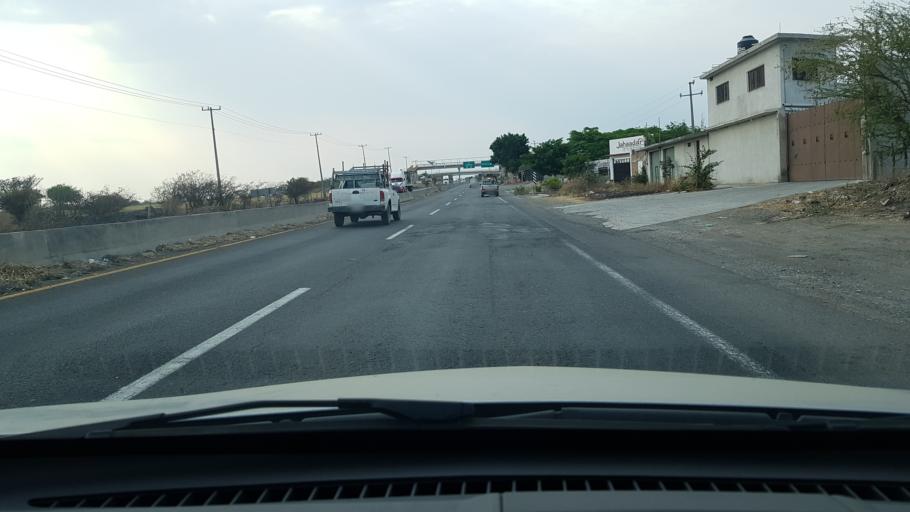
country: MX
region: Morelos
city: Amayuca
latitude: 18.7269
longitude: -98.8084
